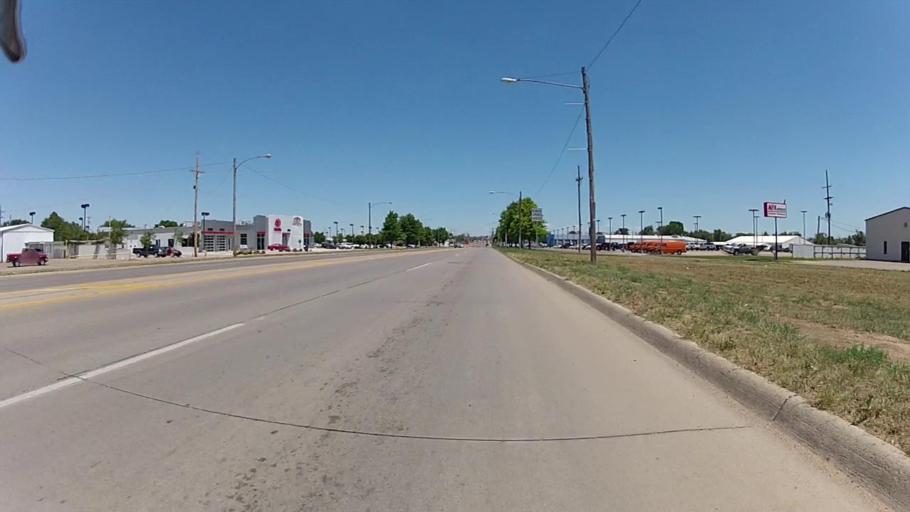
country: US
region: Kansas
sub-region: Ford County
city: Dodge City
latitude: 37.7340
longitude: -100.0194
